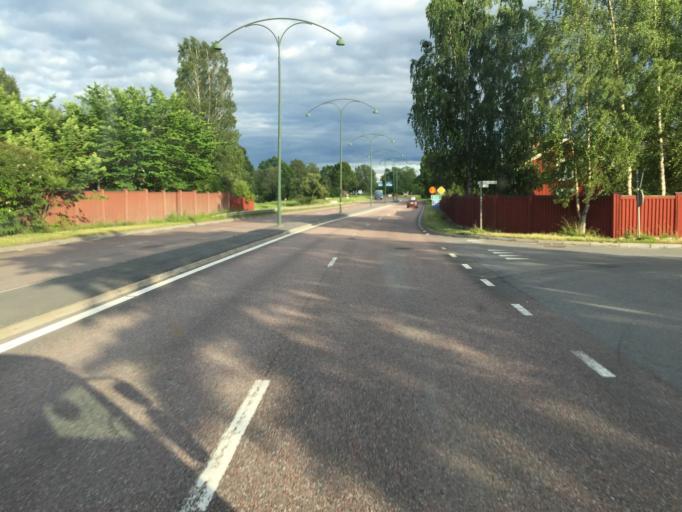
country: SE
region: Dalarna
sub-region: Borlange Kommun
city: Borlaenge
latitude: 60.4981
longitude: 15.3979
